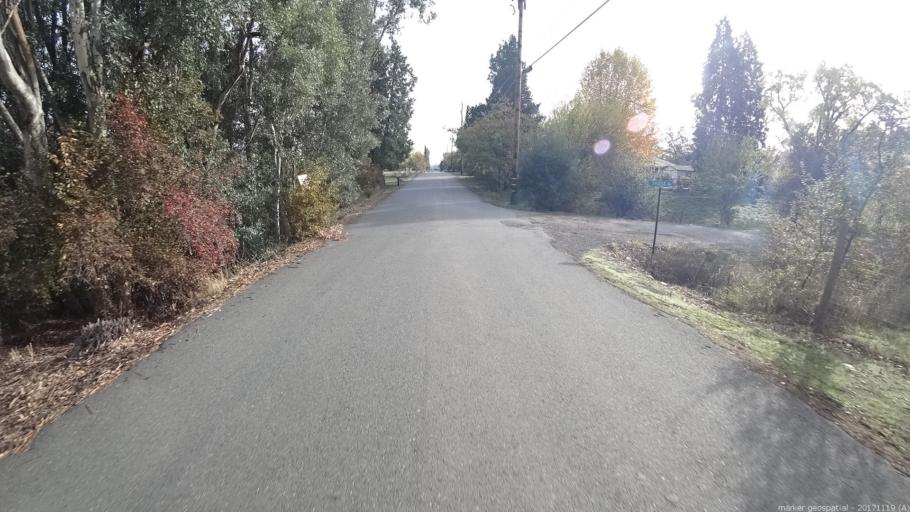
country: US
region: California
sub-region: Shasta County
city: Anderson
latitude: 40.5148
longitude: -122.3395
